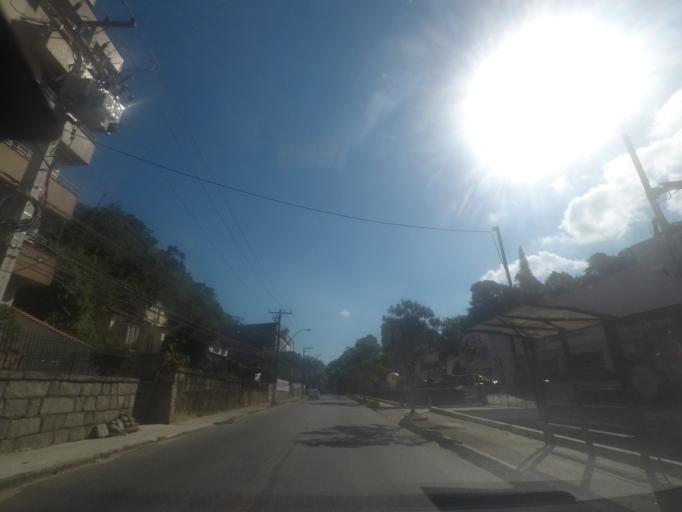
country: BR
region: Rio de Janeiro
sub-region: Petropolis
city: Petropolis
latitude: -22.5263
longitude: -43.1937
